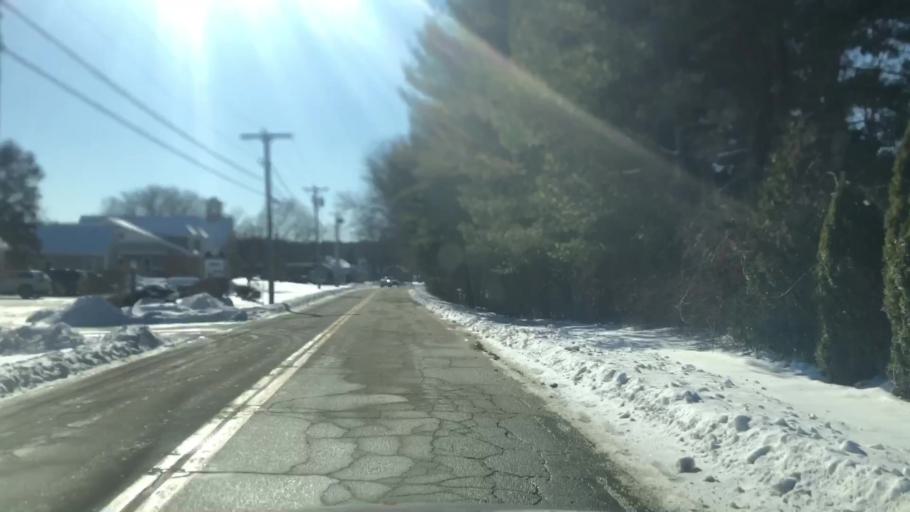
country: US
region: New Hampshire
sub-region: Hillsborough County
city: Bedford
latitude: 42.9421
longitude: -71.5217
